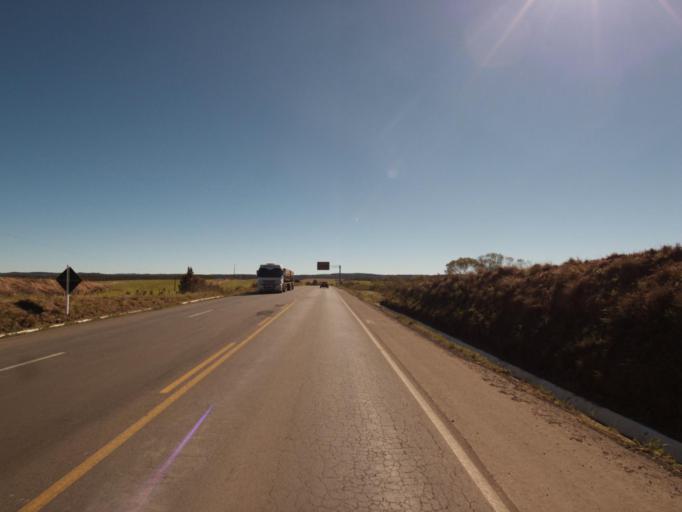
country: BR
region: Santa Catarina
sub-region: Concordia
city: Concordia
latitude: -26.9366
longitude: -51.8693
